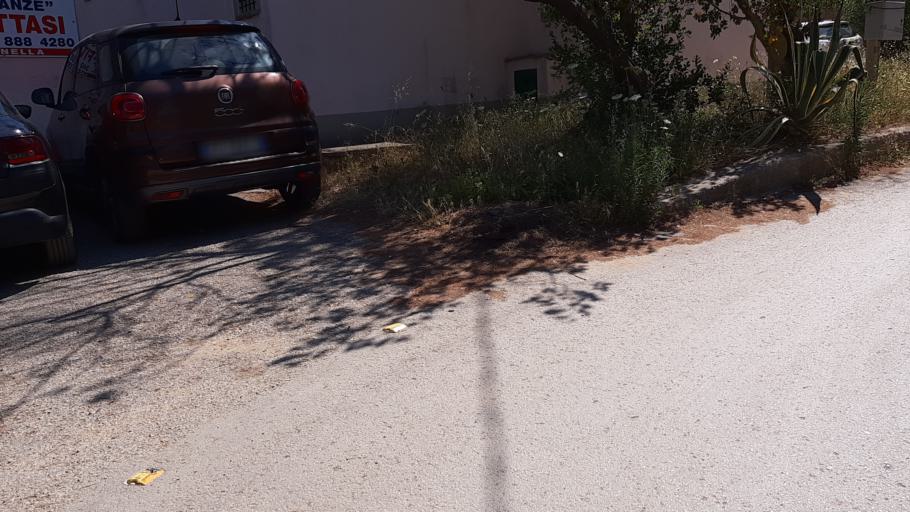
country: IT
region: Tuscany
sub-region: Provincia di Livorno
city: Portoferraio
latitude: 42.7595
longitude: 10.2984
